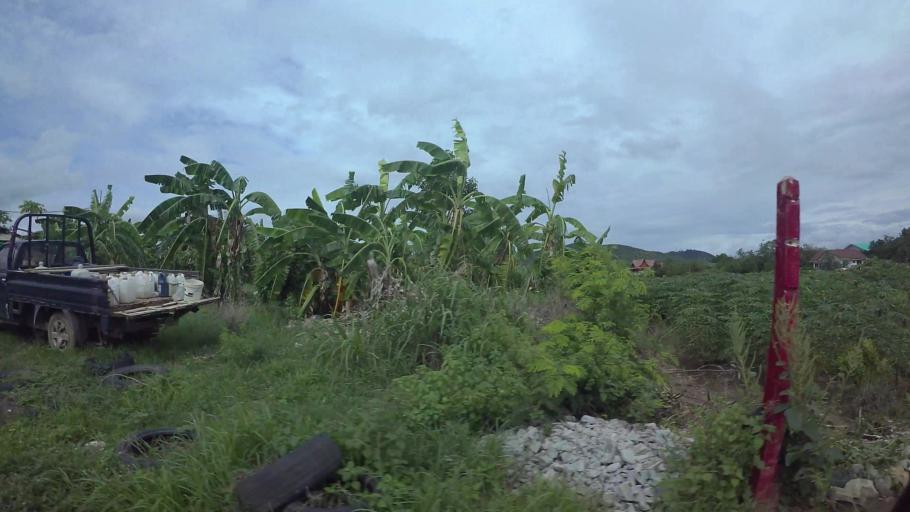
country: TH
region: Chon Buri
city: Sattahip
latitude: 12.7132
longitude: 100.8923
